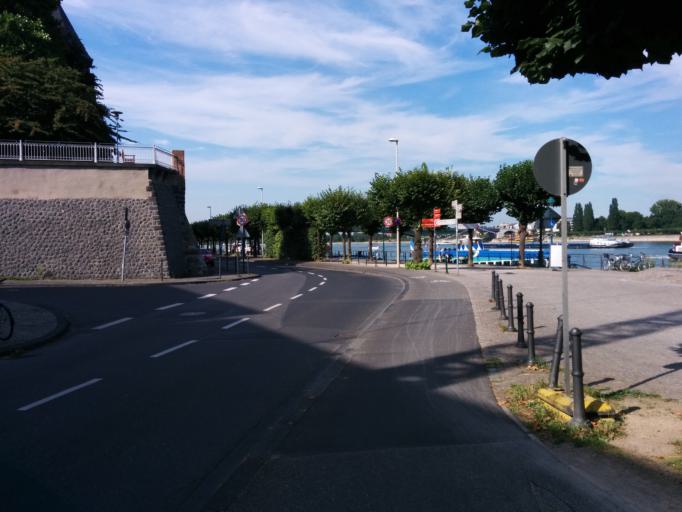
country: DE
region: North Rhine-Westphalia
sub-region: Regierungsbezirk Koln
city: Bonn
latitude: 50.7319
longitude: 7.1093
